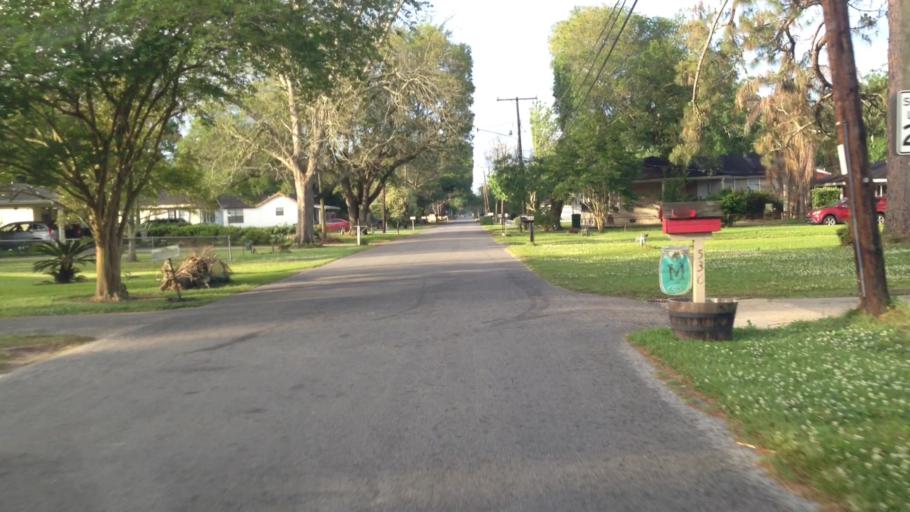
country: US
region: Louisiana
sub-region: Jefferson Parish
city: Bridge City
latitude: 29.9427
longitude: -90.1542
